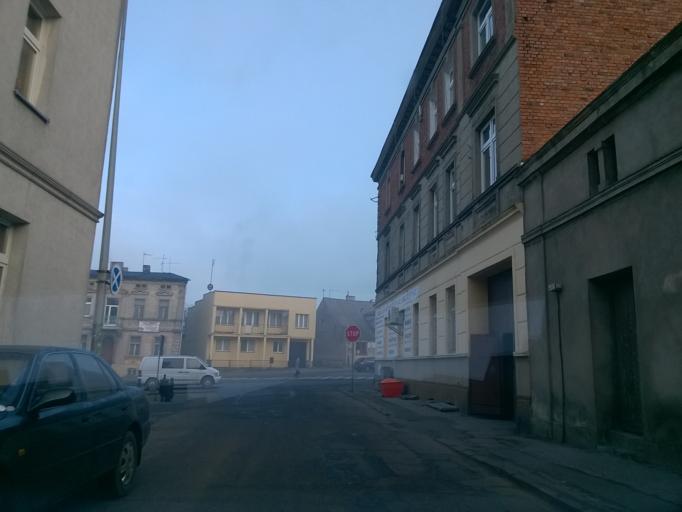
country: PL
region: Kujawsko-Pomorskie
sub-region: Powiat nakielski
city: Kcynia
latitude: 52.9910
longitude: 17.4840
